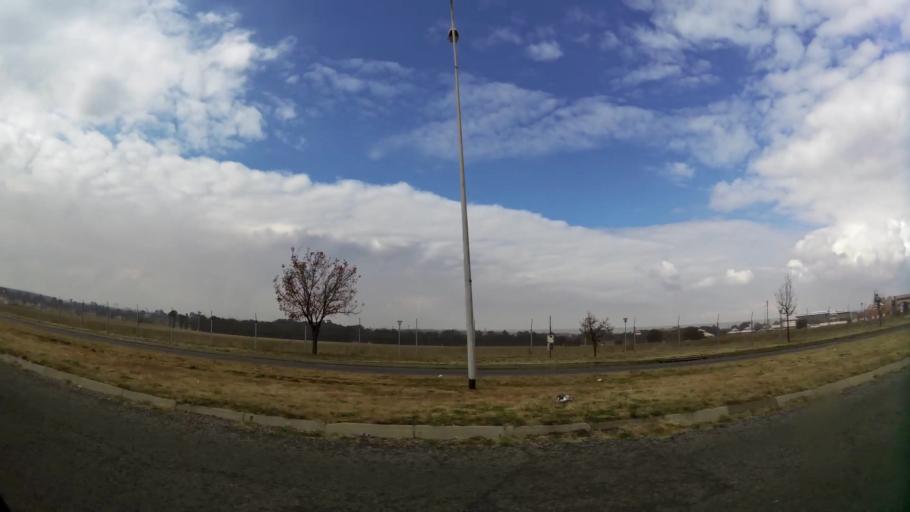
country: ZA
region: Gauteng
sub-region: Sedibeng District Municipality
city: Vanderbijlpark
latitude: -26.7217
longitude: 27.8817
